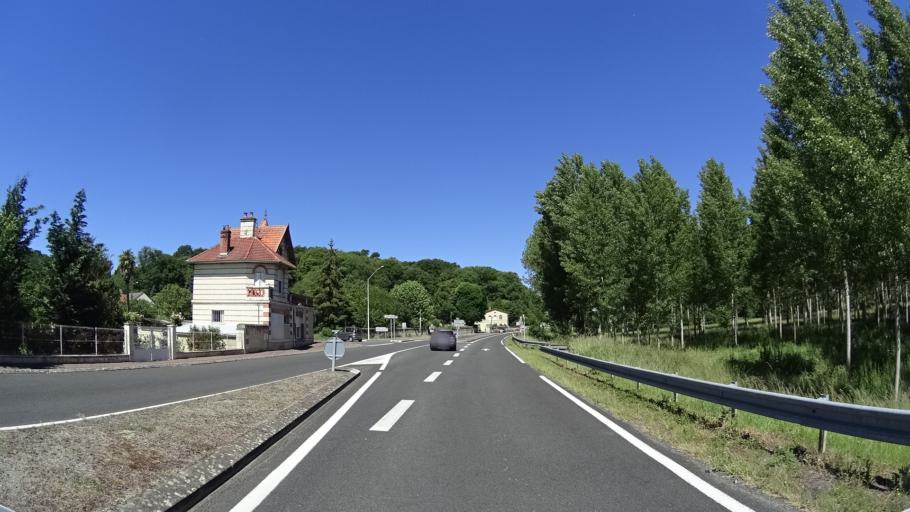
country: FR
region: Pays de la Loire
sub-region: Departement de Maine-et-Loire
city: Saumur
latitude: 47.2797
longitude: -0.1194
